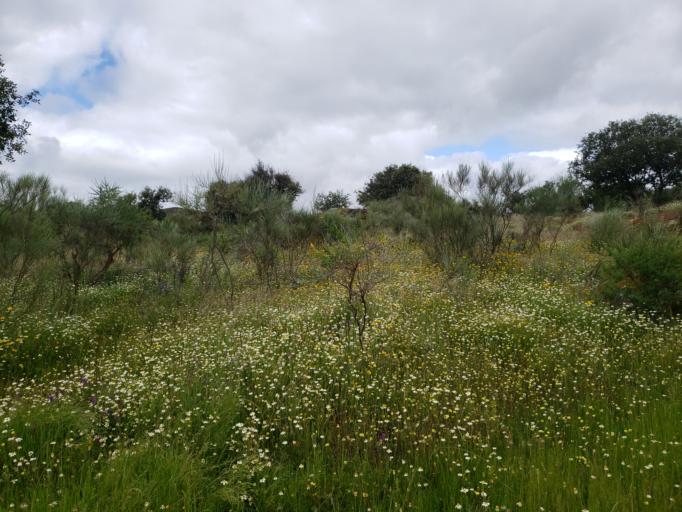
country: ES
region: Extremadura
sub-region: Provincia de Caceres
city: Malpartida de Caceres
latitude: 39.4262
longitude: -6.4946
